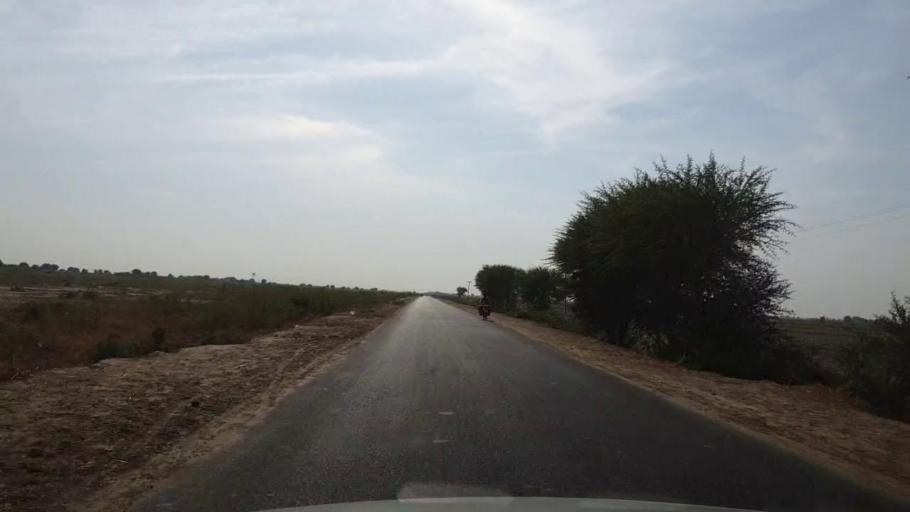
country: PK
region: Sindh
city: Kunri
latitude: 25.1620
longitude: 69.5072
